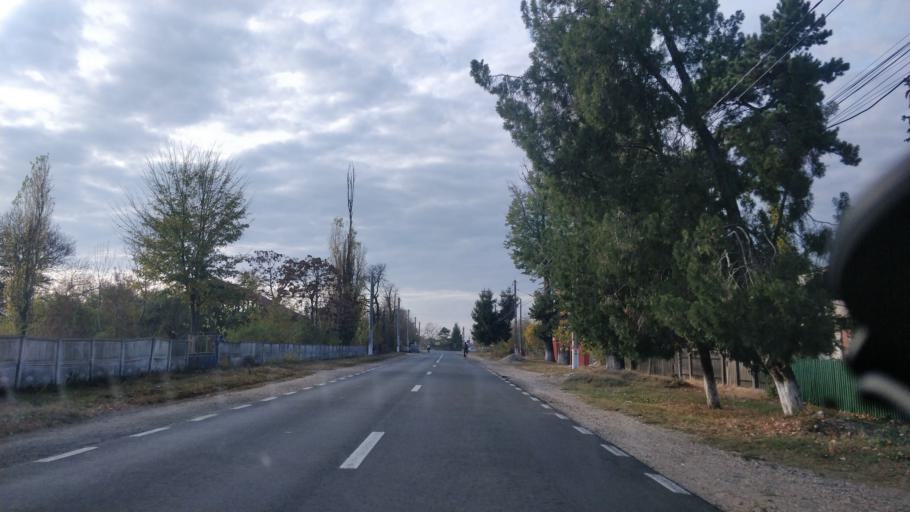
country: RO
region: Giurgiu
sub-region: Comuna Clejani
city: Clejani
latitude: 44.3425
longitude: 25.6738
